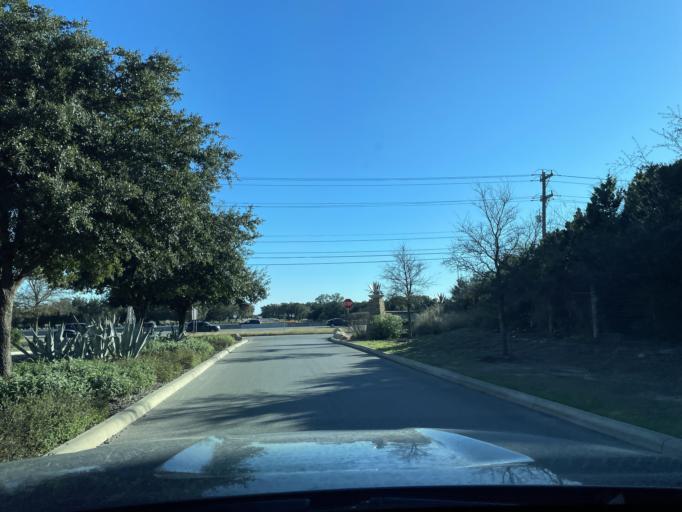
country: US
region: Texas
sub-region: Bexar County
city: Shavano Park
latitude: 29.5907
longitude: -98.6082
